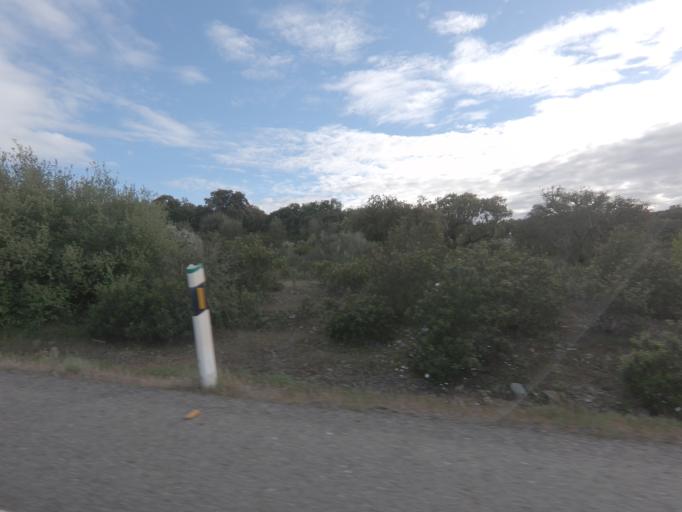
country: ES
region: Extremadura
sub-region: Provincia de Caceres
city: Pedroso de Acim
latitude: 39.8284
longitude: -6.3798
